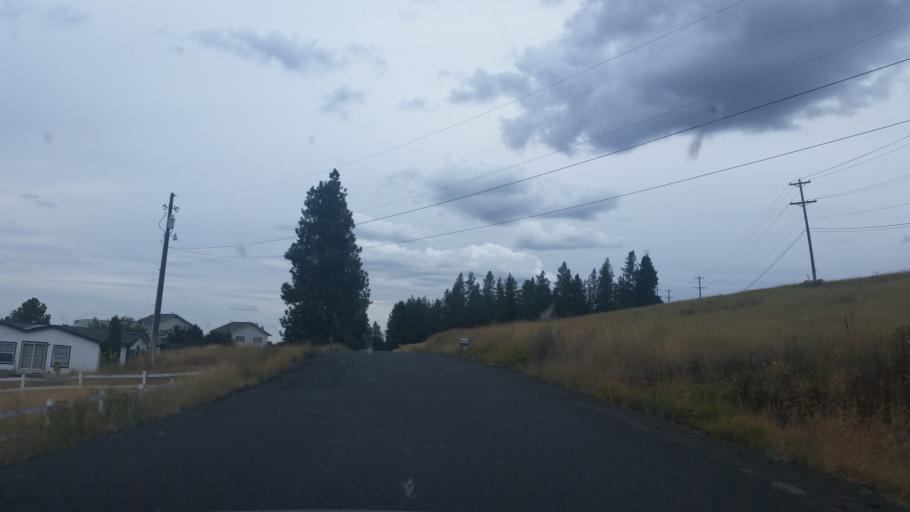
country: US
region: Washington
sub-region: Spokane County
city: Cheney
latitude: 47.5191
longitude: -117.5752
